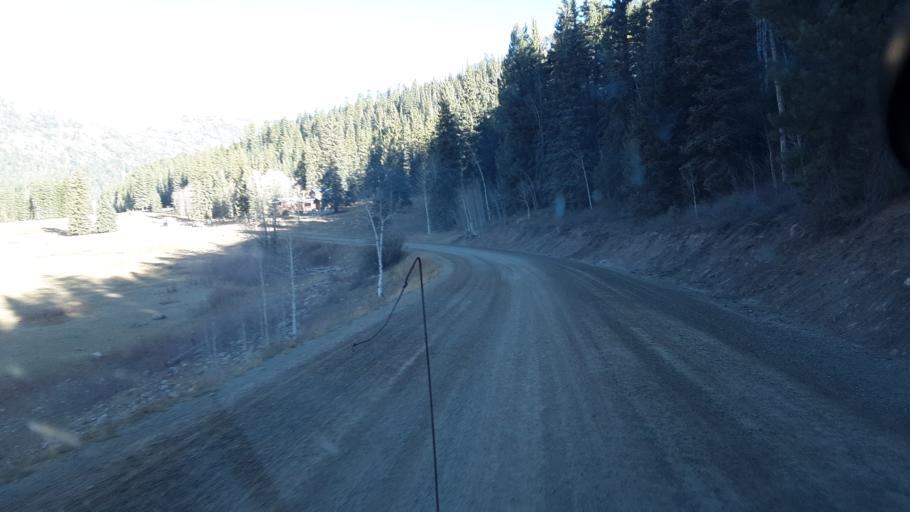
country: US
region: Colorado
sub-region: La Plata County
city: Bayfield
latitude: 37.4203
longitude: -107.6667
